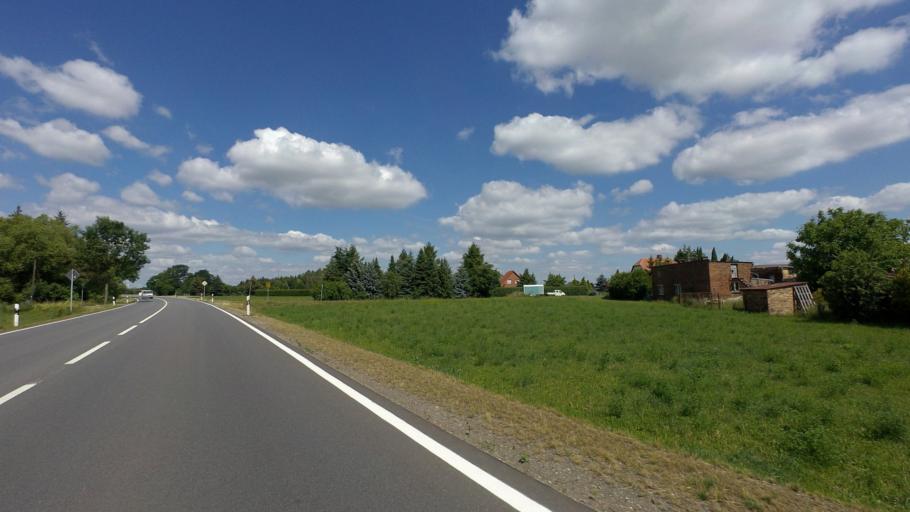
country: DE
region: Brandenburg
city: Sallgast
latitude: 51.6051
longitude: 13.8823
